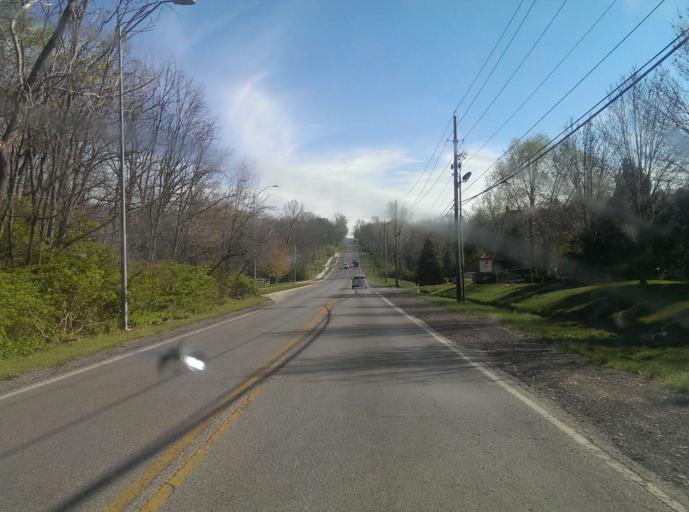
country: US
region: Kansas
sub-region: Johnson County
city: Leawood
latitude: 38.9084
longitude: -94.5939
